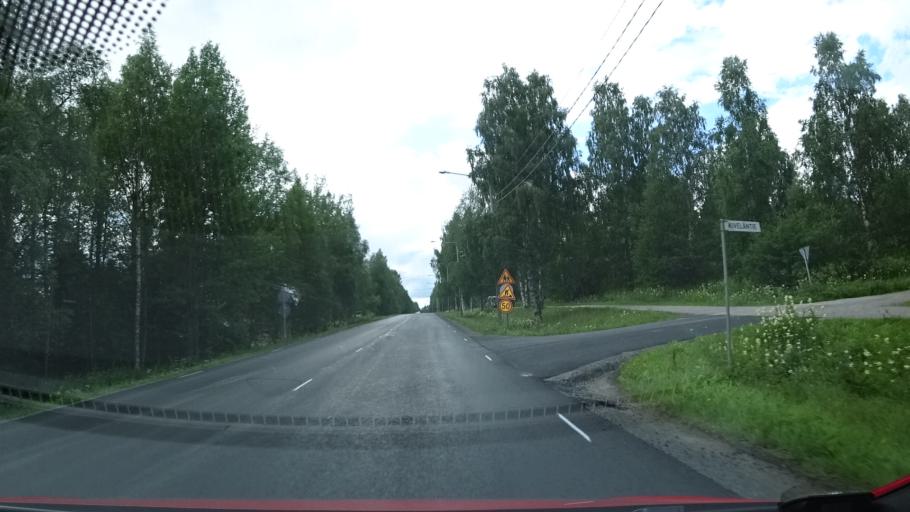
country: FI
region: Lapland
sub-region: Rovaniemi
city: Rovaniemi
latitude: 66.4317
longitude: 25.4777
